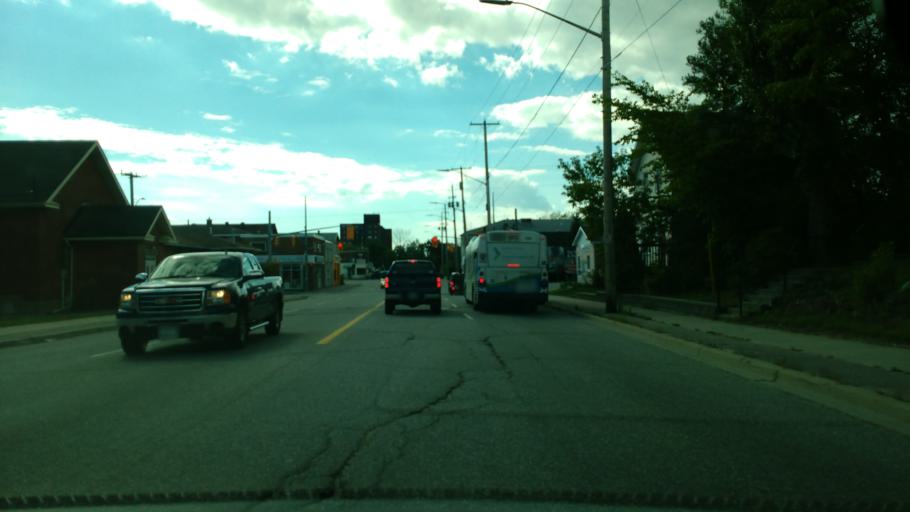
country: CA
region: Ontario
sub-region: Nipissing District
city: North Bay
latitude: 46.3180
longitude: -79.4539
